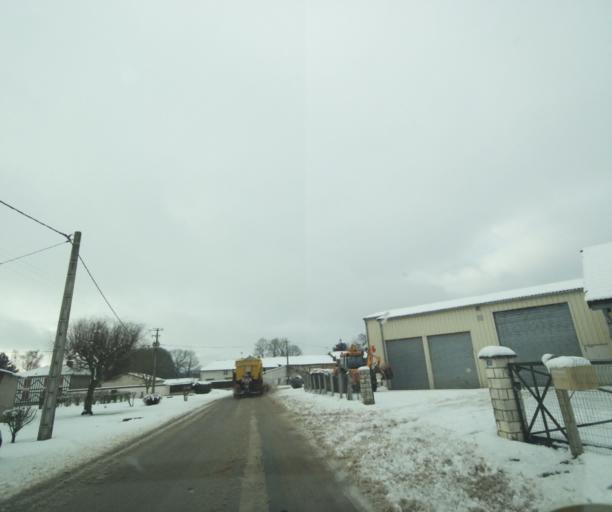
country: FR
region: Champagne-Ardenne
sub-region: Departement de la Haute-Marne
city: Montier-en-Der
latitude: 48.4910
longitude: 4.6992
